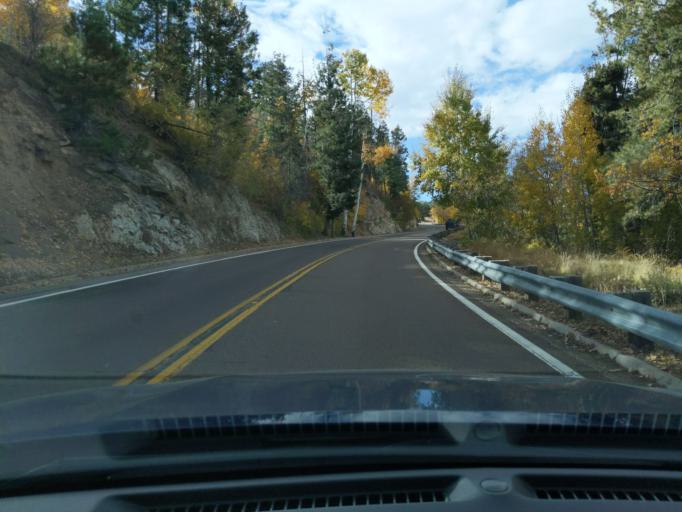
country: US
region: Arizona
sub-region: Pima County
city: Tanque Verde
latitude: 32.4316
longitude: -110.7475
